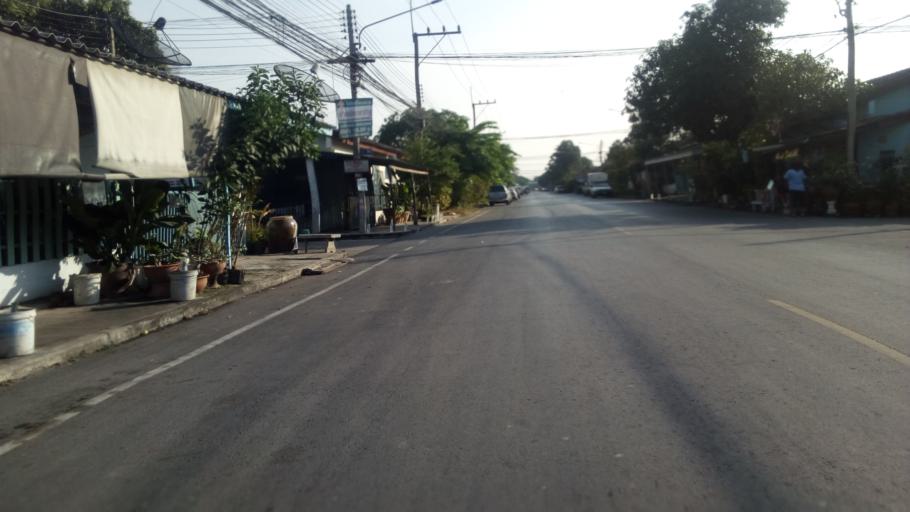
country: TH
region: Pathum Thani
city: Nong Suea
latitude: 14.0516
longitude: 100.8564
